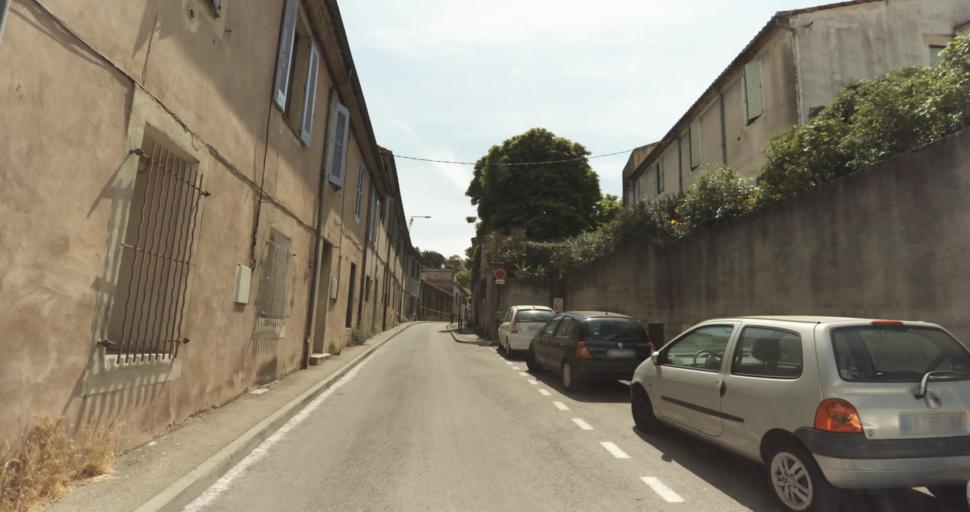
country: FR
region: Languedoc-Roussillon
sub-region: Departement du Gard
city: Nimes
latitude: 43.8475
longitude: 4.3626
